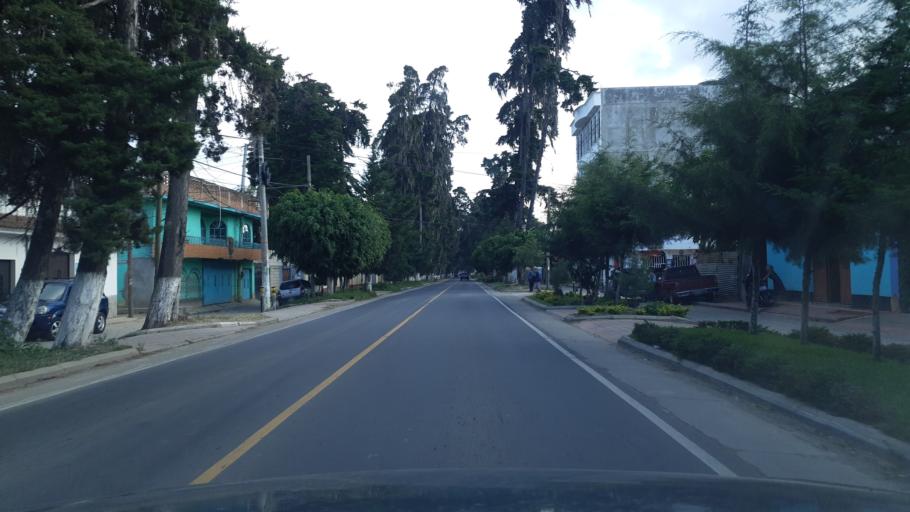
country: GT
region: Chimaltenango
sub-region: Municipio de Chimaltenango
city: Chimaltenango
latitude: 14.6497
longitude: -90.8140
